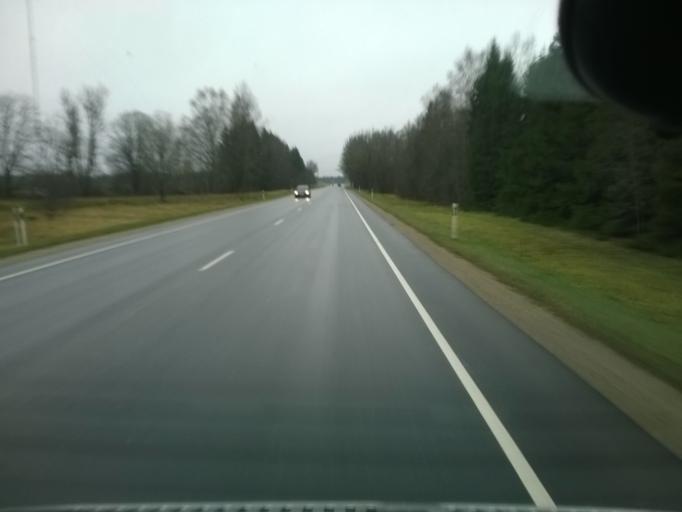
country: EE
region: Harju
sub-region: Nissi vald
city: Turba
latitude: 59.0443
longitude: 24.1714
